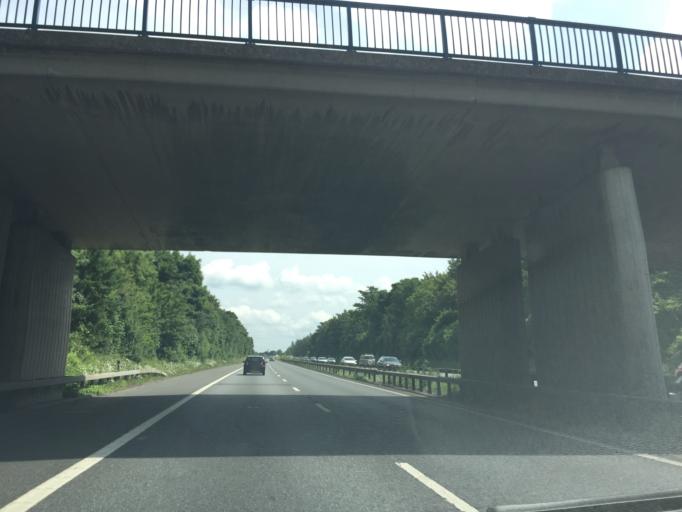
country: GB
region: England
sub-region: Kent
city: Sittingbourne
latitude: 51.3167
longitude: 0.6987
